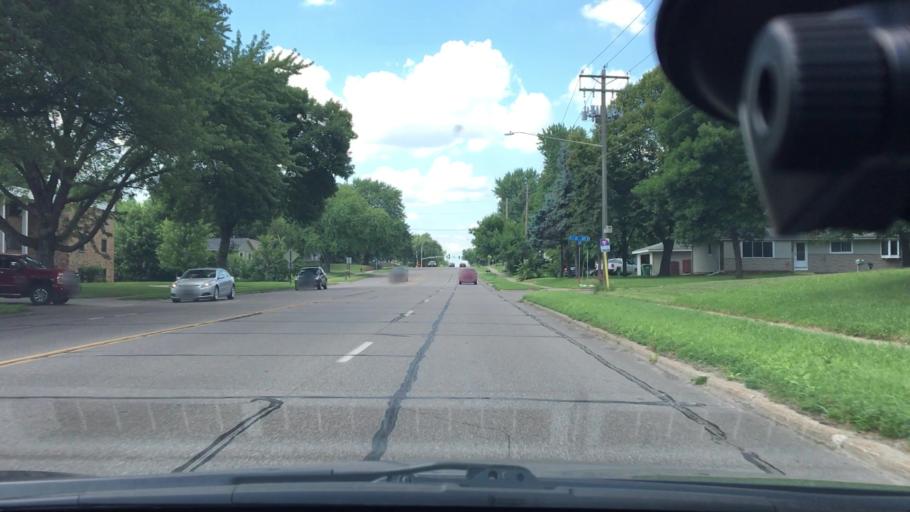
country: US
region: Minnesota
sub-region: Hennepin County
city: New Hope
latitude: 45.0370
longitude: -93.3803
